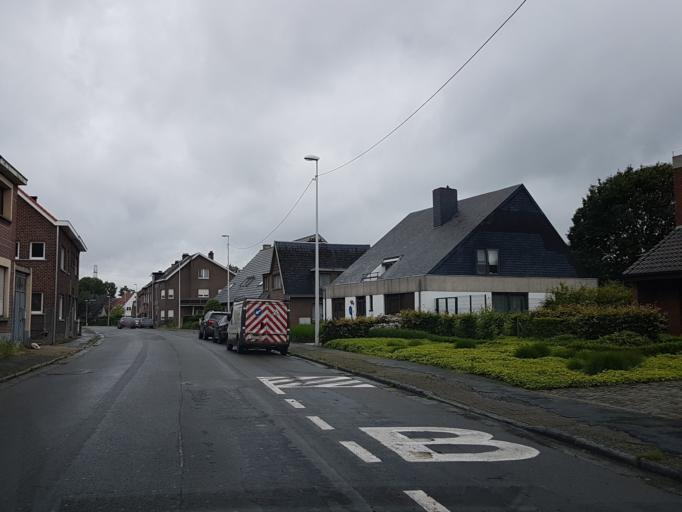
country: BE
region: Flanders
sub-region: Provincie Oost-Vlaanderen
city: Aalst
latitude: 50.9569
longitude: 4.0489
